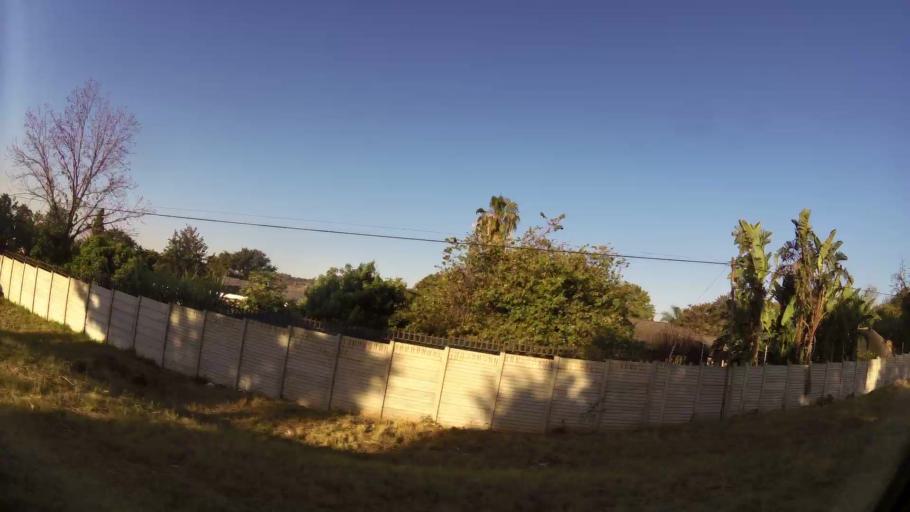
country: ZA
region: North-West
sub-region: Bojanala Platinum District Municipality
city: Rustenburg
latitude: -25.6979
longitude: 27.2187
